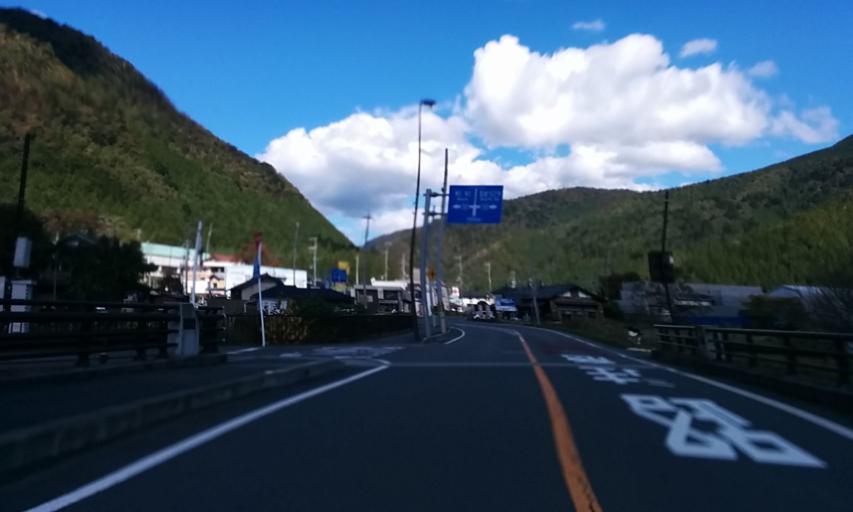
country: JP
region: Kyoto
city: Kameoka
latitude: 35.2741
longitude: 135.5509
